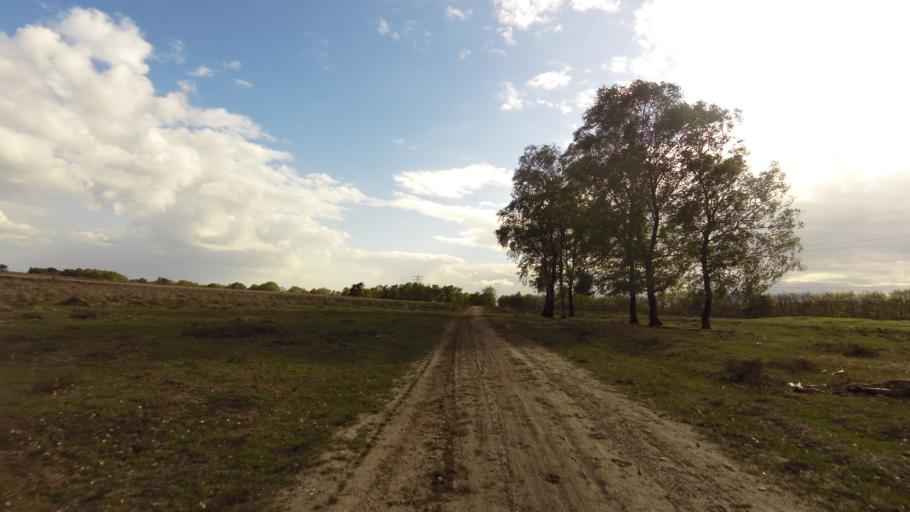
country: NL
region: Gelderland
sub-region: Gemeente Rozendaal
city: Rozendaal
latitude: 52.0652
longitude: 5.9466
